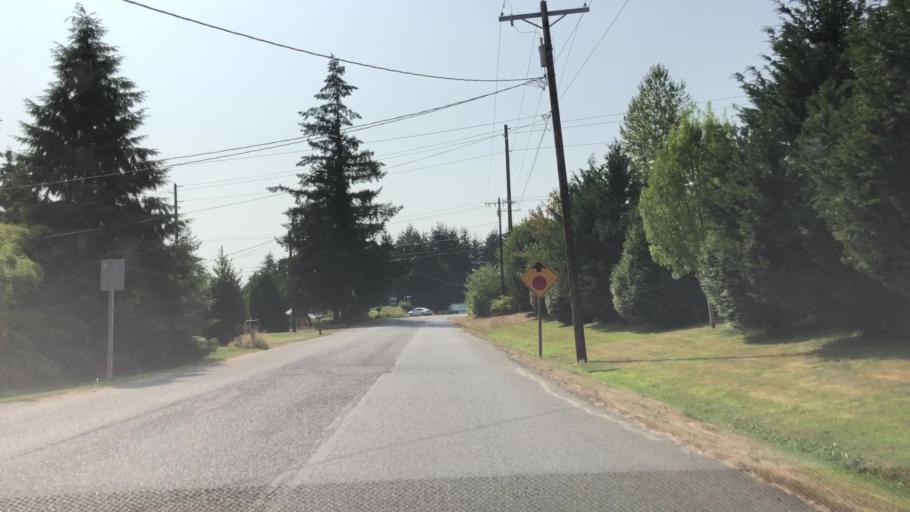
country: US
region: Washington
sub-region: Snohomish County
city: Lochsloy
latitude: 48.0541
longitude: -122.0285
